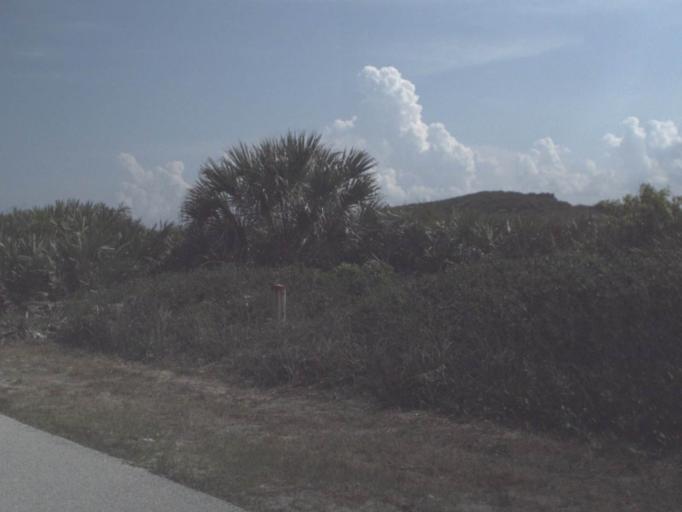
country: US
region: Florida
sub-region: Saint Johns County
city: Villano Beach
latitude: 30.0393
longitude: -81.3276
